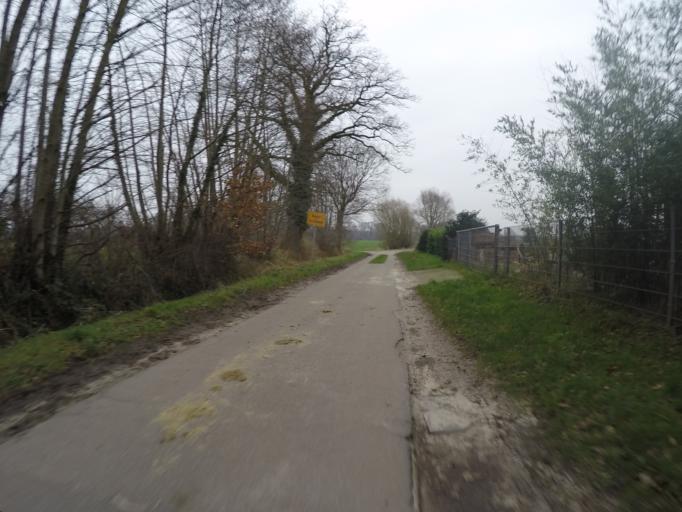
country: DE
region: Schleswig-Holstein
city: Borstel-Hohenraden
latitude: 53.7013
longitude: 9.8335
